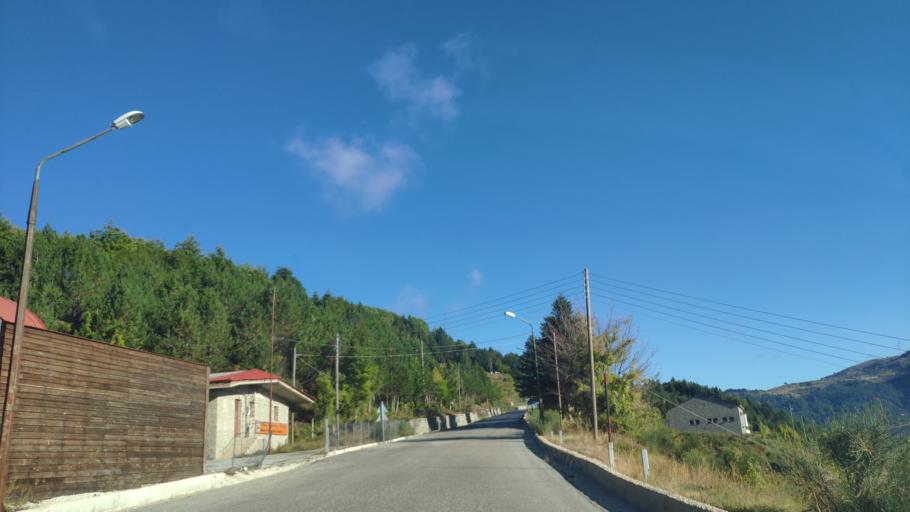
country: GR
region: Epirus
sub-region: Nomos Ioanninon
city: Metsovo
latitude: 39.7705
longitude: 21.1762
